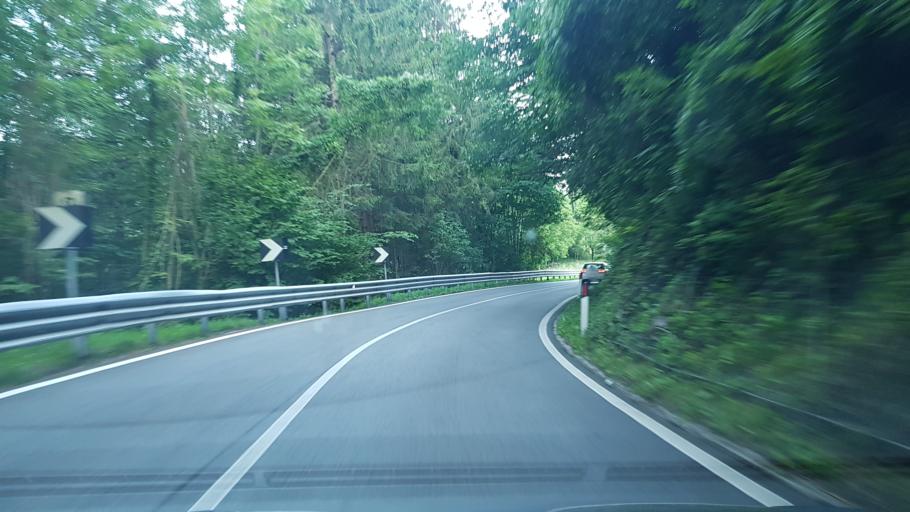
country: IT
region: Friuli Venezia Giulia
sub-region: Provincia di Udine
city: Rigolato
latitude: 46.5403
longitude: 12.8645
